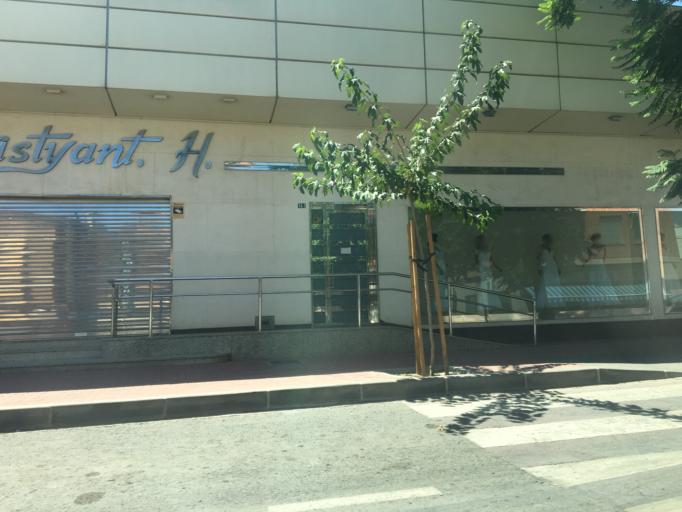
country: ES
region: Murcia
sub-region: Murcia
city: Murcia
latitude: 38.0049
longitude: -1.1155
